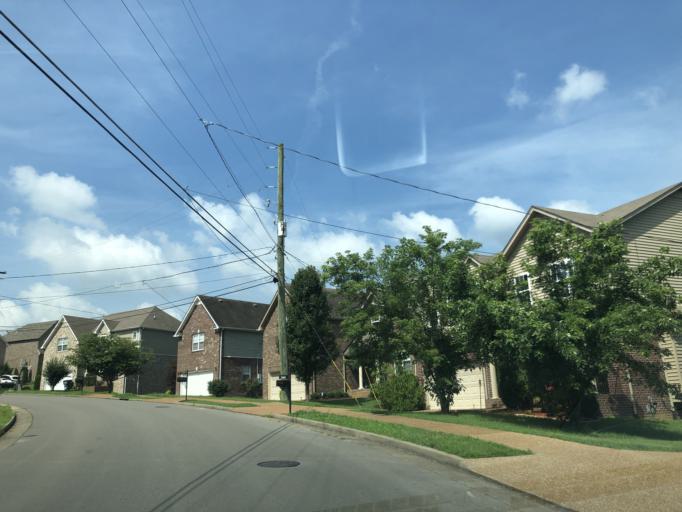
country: US
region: Tennessee
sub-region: Williamson County
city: Nolensville
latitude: 36.0106
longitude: -86.6871
